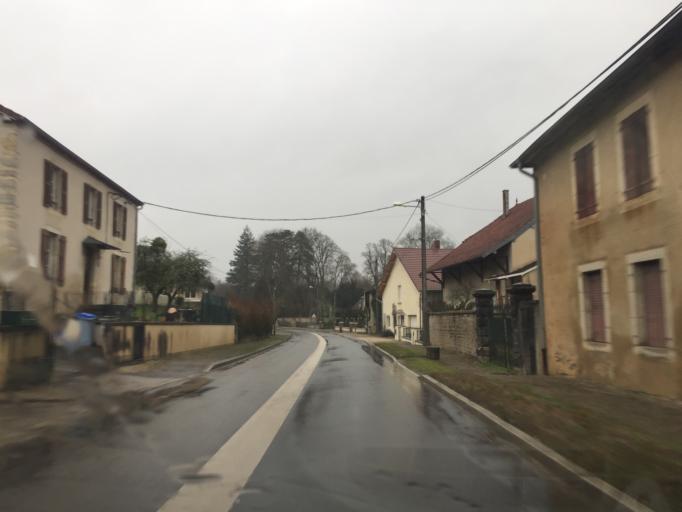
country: FR
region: Franche-Comte
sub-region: Departement du Doubs
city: Arc-et-Senans
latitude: 46.9990
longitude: 5.7546
